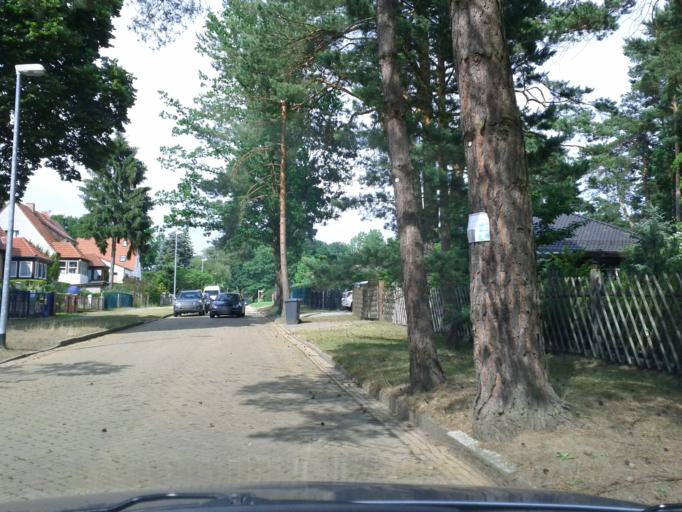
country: DE
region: Brandenburg
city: Schoneiche
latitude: 52.4652
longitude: 13.7072
